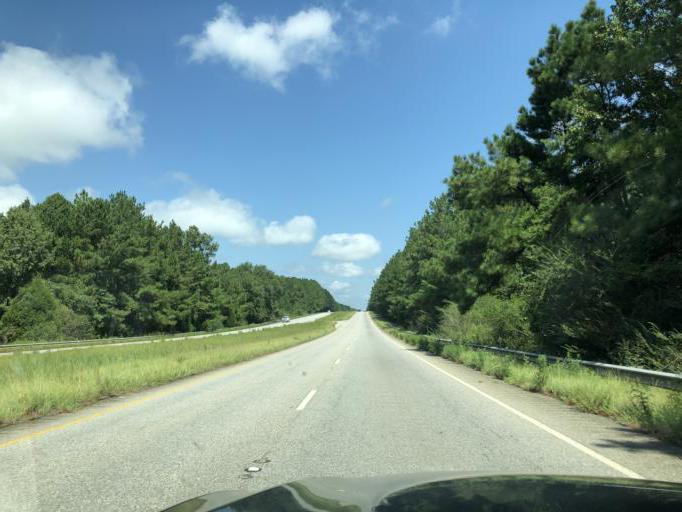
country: US
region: Alabama
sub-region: Henry County
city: Abbeville
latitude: 31.6420
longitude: -85.2807
